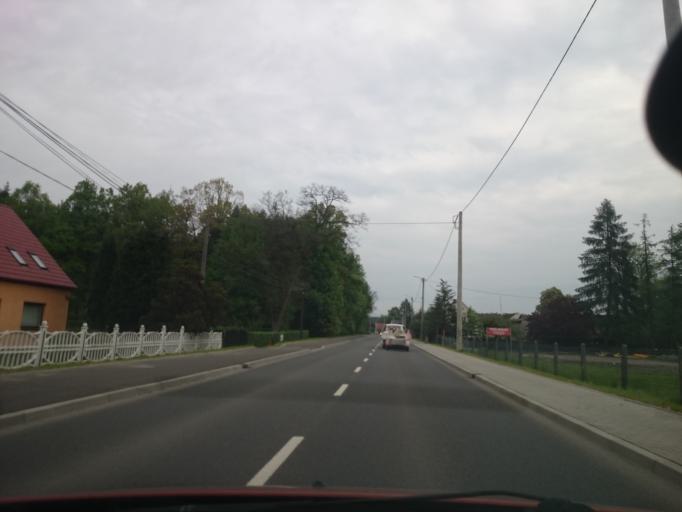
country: PL
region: Opole Voivodeship
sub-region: Powiat opolski
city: Kup
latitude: 50.8128
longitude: 17.8820
